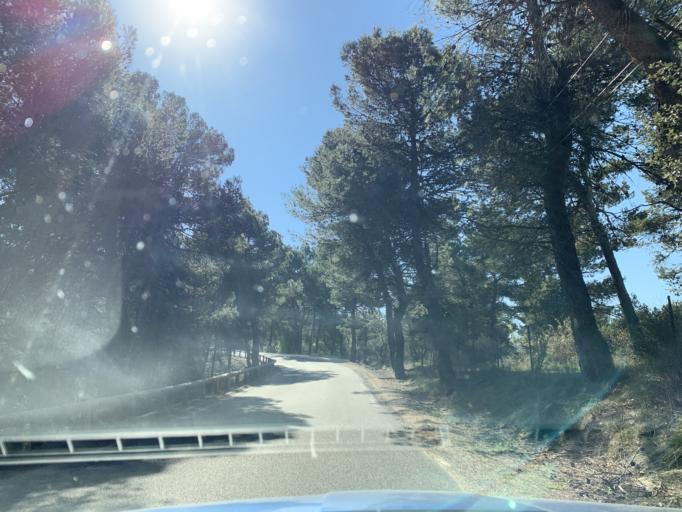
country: FR
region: Provence-Alpes-Cote d'Azur
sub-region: Departement du Vaucluse
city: Goult
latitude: 43.8791
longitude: 5.2624
